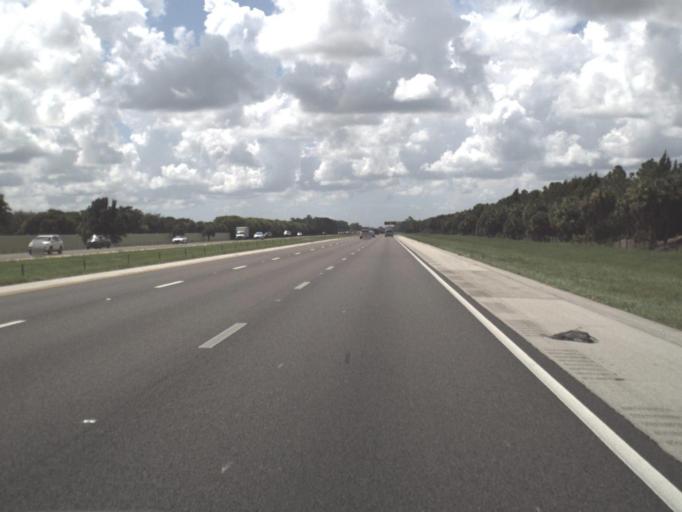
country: US
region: Florida
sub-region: Lee County
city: Bonita Springs
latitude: 26.3027
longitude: -81.7431
